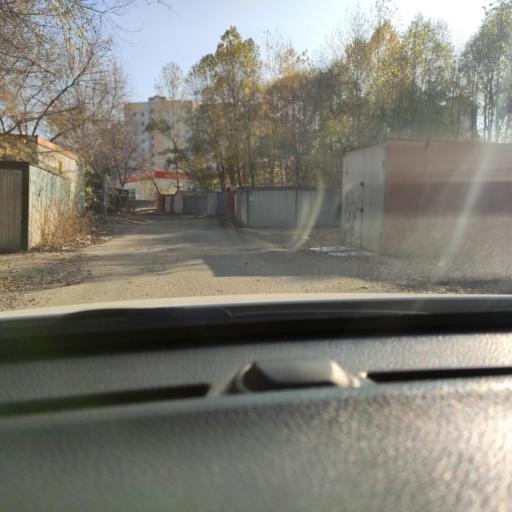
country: RU
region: Voronezj
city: Voronezh
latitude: 51.7212
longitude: 39.2617
